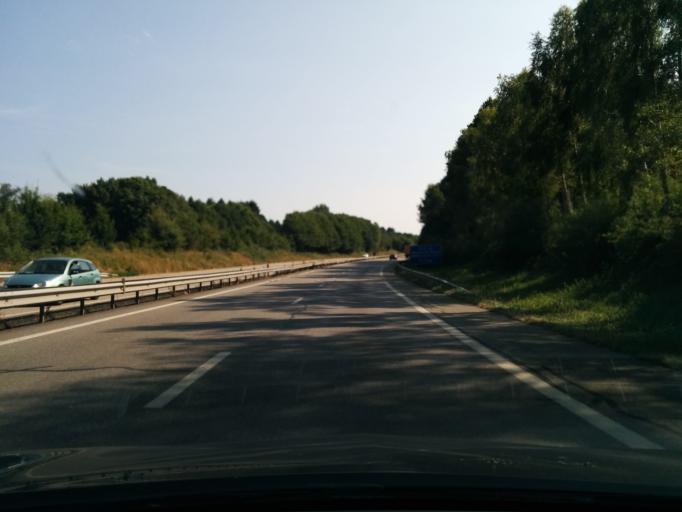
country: FR
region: Limousin
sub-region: Departement de la Haute-Vienne
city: Bonnac-la-Cote
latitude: 45.9265
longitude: 1.3027
